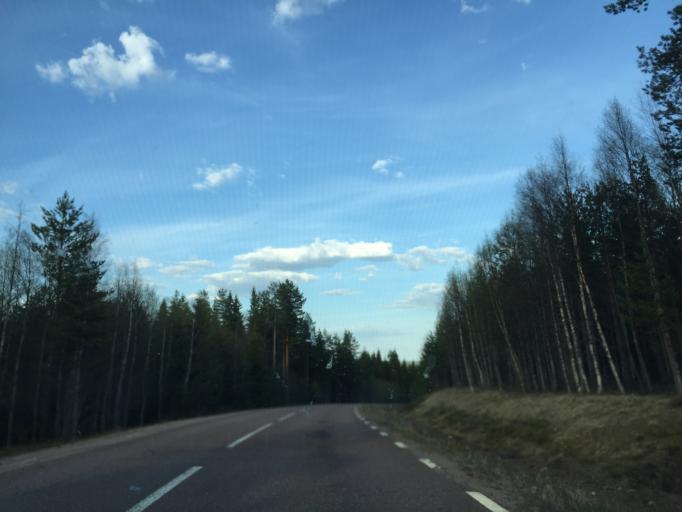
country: SE
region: Dalarna
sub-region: Leksand Municipality
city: Siljansnas
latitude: 60.6711
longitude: 14.6395
